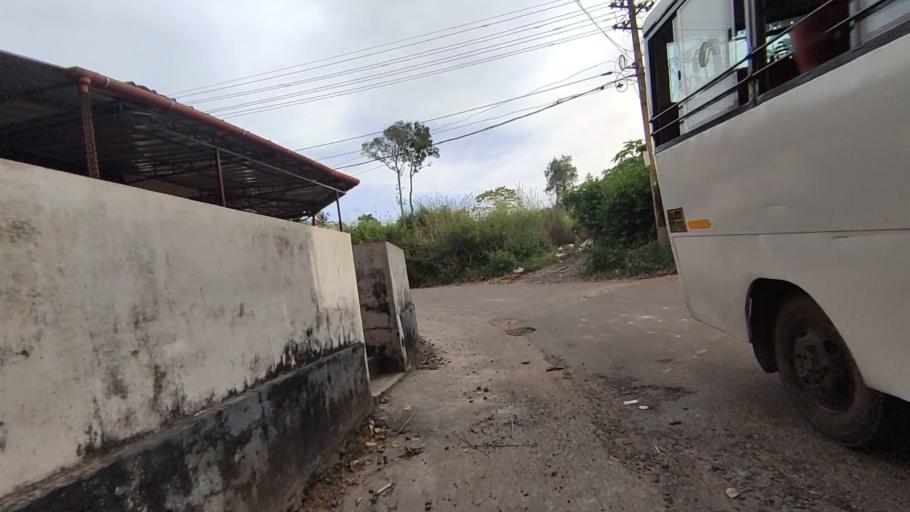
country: IN
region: Kerala
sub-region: Kottayam
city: Kottayam
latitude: 9.6100
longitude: 76.4863
